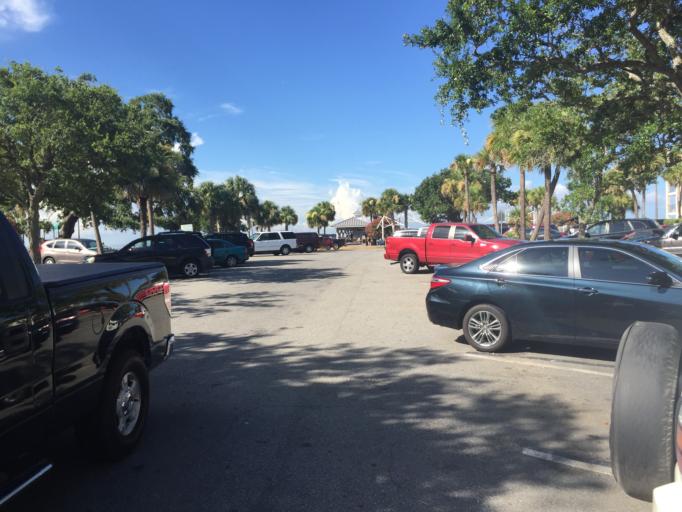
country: US
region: Georgia
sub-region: Glynn County
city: Saint Simons Island
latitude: 31.1350
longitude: -81.3962
